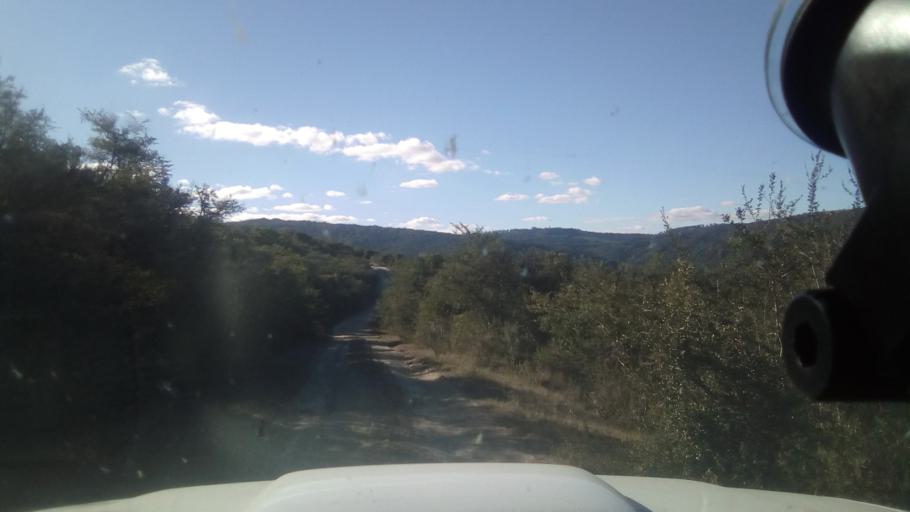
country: ZA
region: Eastern Cape
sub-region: Buffalo City Metropolitan Municipality
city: Bhisho
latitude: -32.7388
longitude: 27.3479
